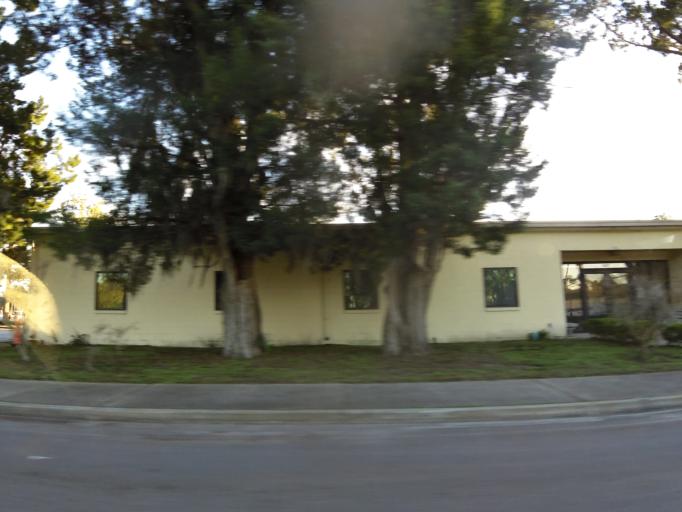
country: US
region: Florida
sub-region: Duval County
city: Jacksonville
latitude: 30.3396
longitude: -81.7092
